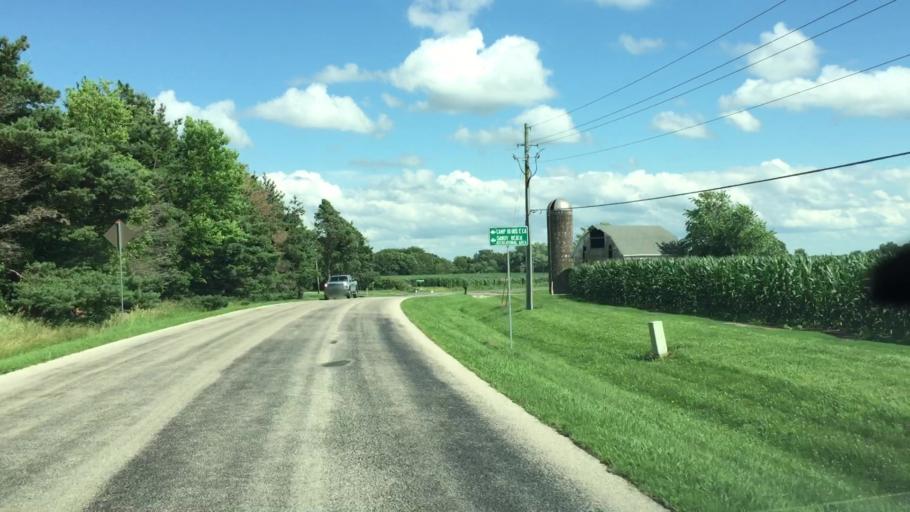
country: US
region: Iowa
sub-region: Linn County
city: Ely
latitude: 41.8158
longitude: -91.6177
